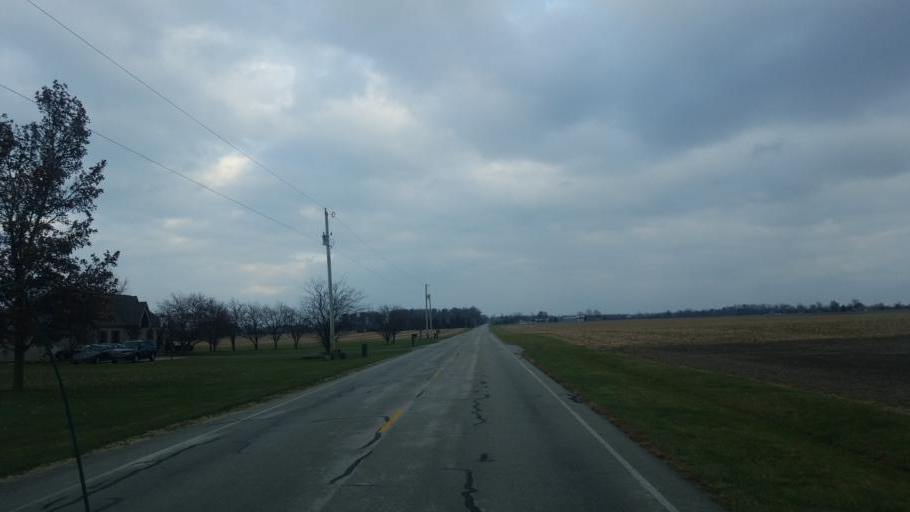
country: US
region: Ohio
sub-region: Mercer County
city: Coldwater
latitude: 40.5090
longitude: -84.6207
